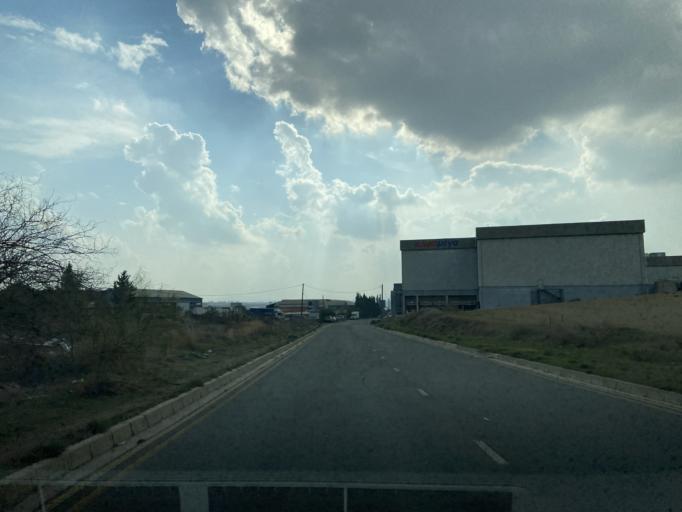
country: CY
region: Lefkosia
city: Dali
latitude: 35.0600
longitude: 33.3954
